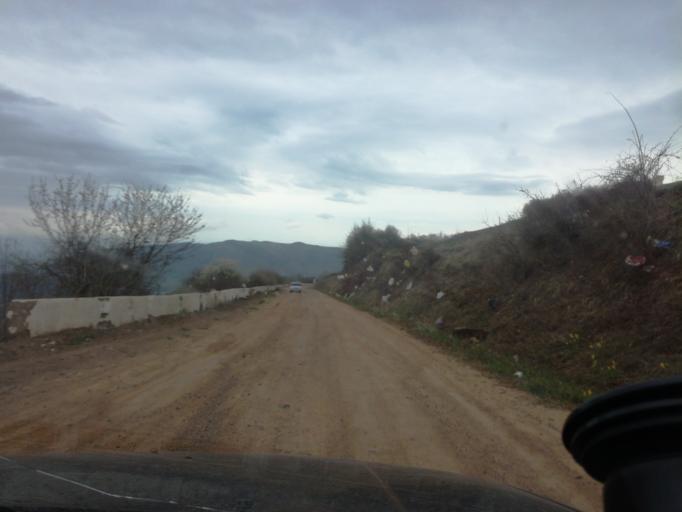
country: AM
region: Tavush
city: Mosesgegh
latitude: 40.8907
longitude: 45.4642
